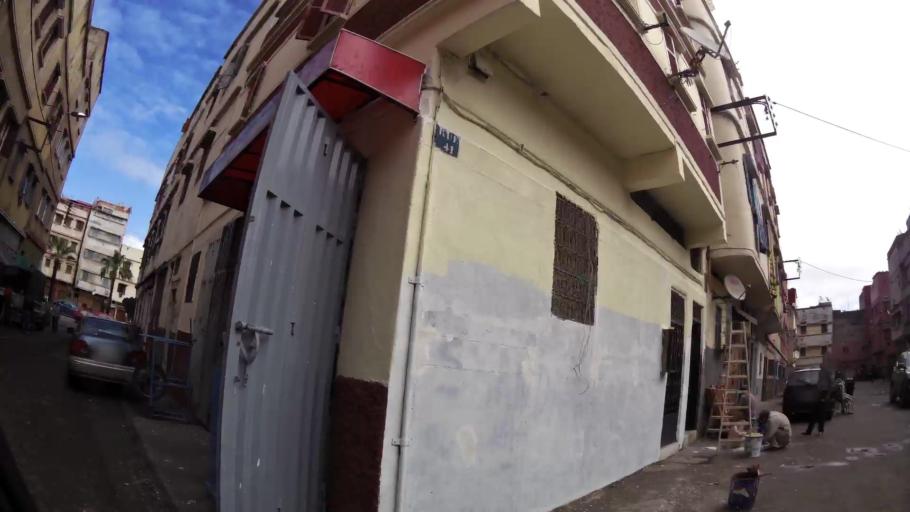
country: MA
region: Grand Casablanca
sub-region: Casablanca
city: Casablanca
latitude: 33.5676
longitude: -7.5851
